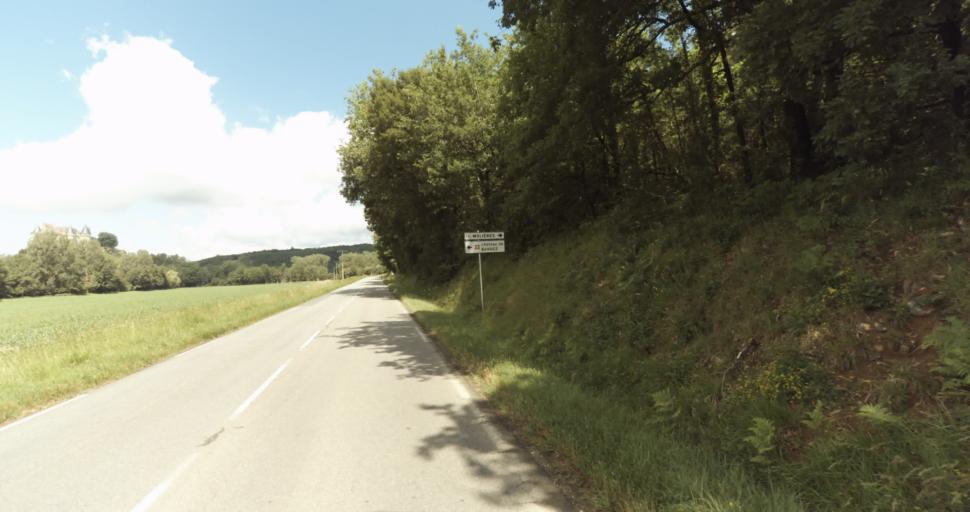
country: FR
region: Aquitaine
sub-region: Departement de la Dordogne
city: Beaumont-du-Perigord
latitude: 44.7931
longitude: 0.7565
